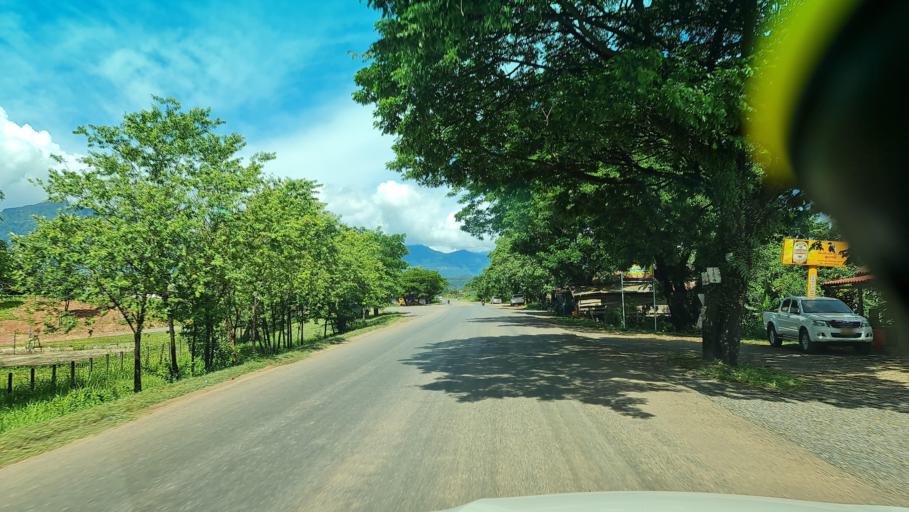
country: LA
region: Bolikhamxai
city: Ban Nahin
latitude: 18.3006
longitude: 104.1154
